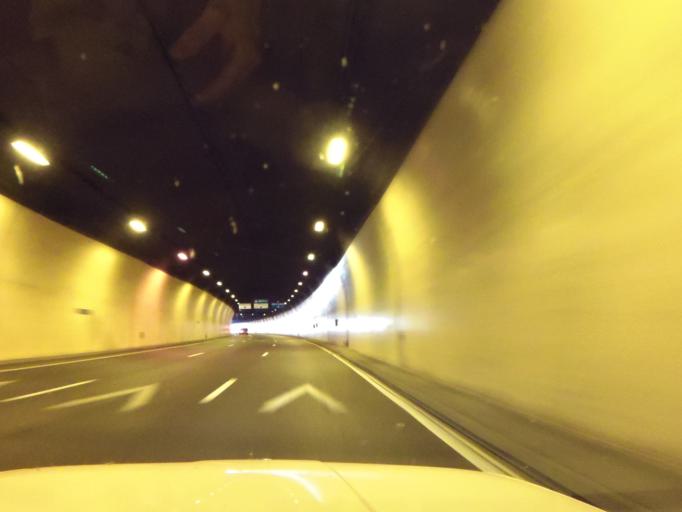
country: FR
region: Rhone-Alpes
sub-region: Departement du Rhone
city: Ecully
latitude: 45.7771
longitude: 4.7916
